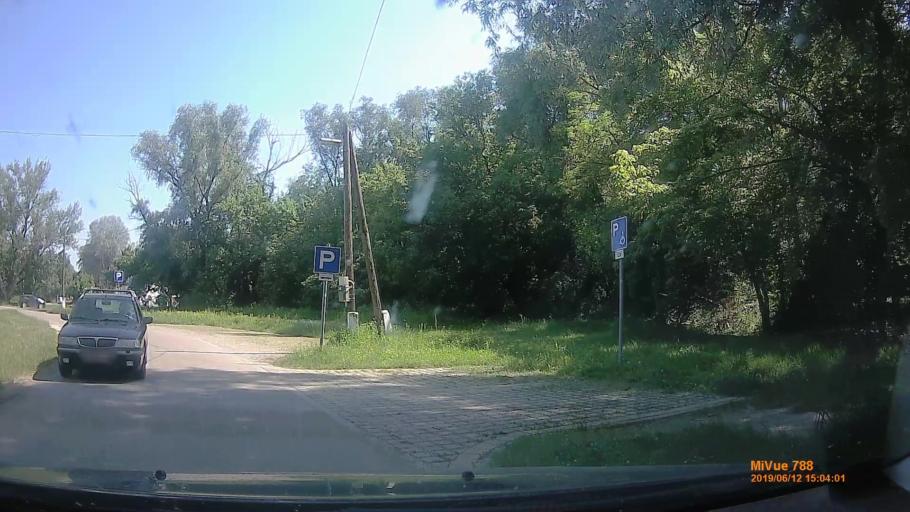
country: HU
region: Csongrad
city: Mako
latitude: 46.2001
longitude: 20.4667
